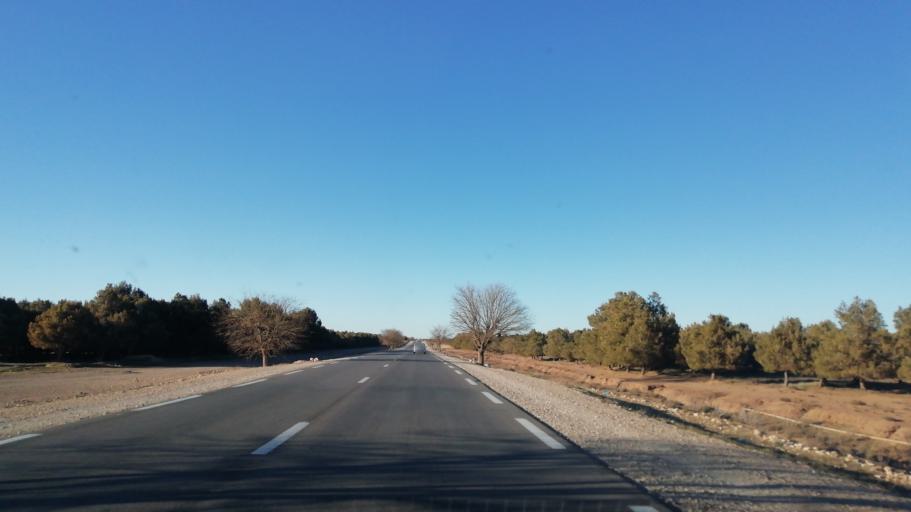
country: DZ
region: Tlemcen
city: Sebdou
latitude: 34.5111
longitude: -1.2832
